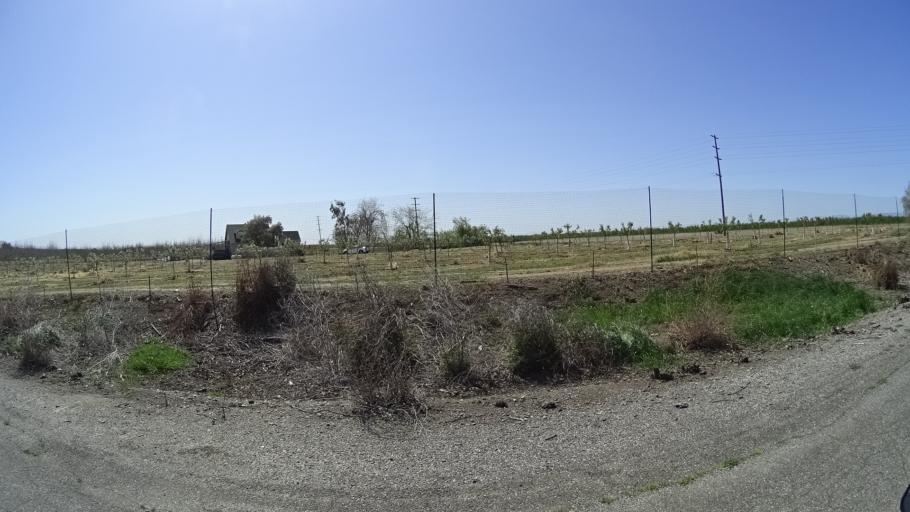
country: US
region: California
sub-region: Glenn County
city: Hamilton City
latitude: 39.7755
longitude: -122.0374
